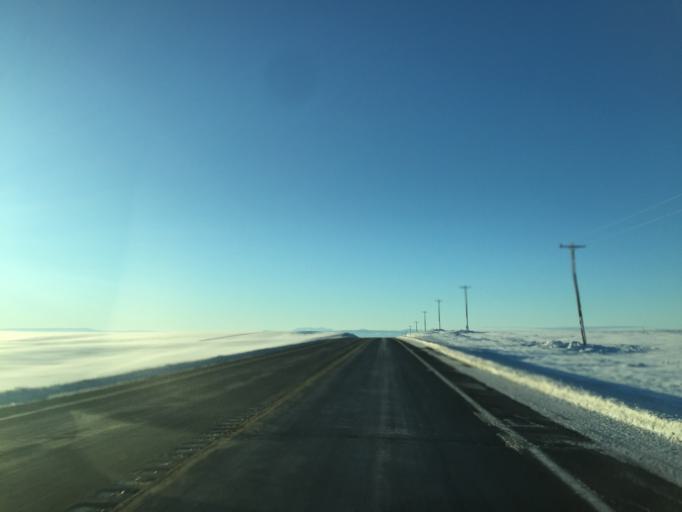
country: US
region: Washington
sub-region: Grant County
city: Soap Lake
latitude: 47.5994
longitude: -119.5677
